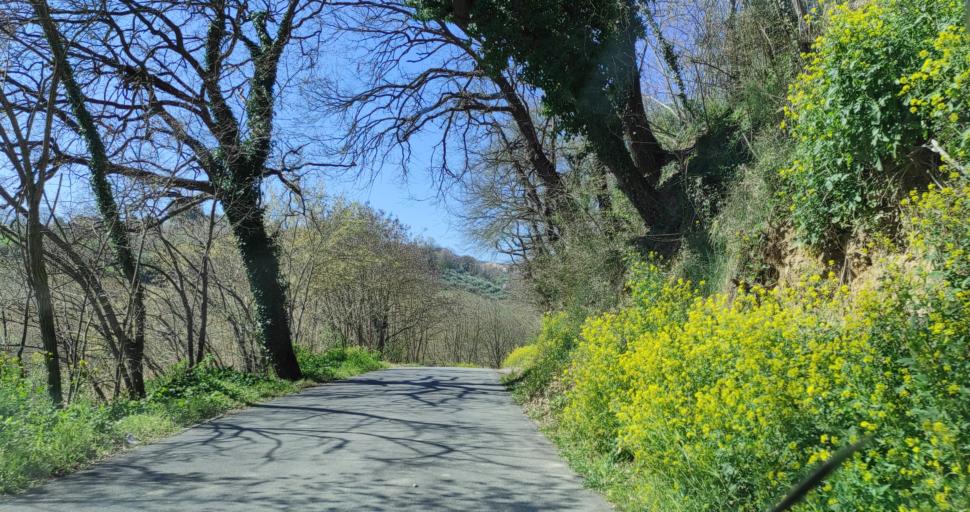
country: IT
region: The Marches
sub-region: Provincia di Macerata
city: Macerata
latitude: 43.3118
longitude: 13.4802
